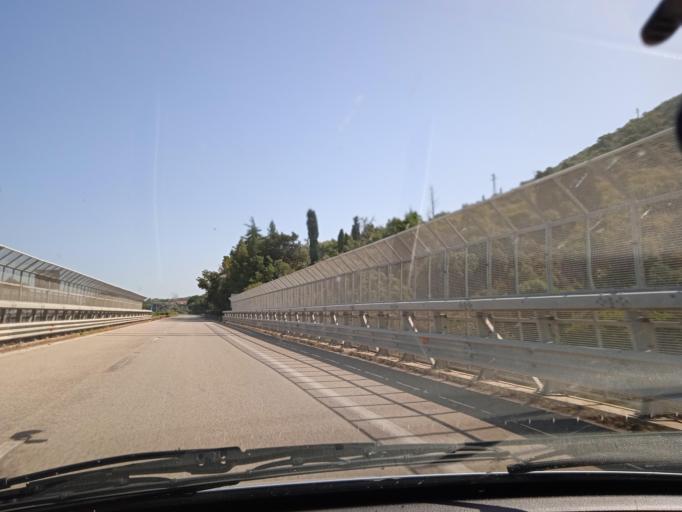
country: IT
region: Sicily
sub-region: Messina
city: Rocca di Capri Leone
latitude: 38.1117
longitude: 14.7236
